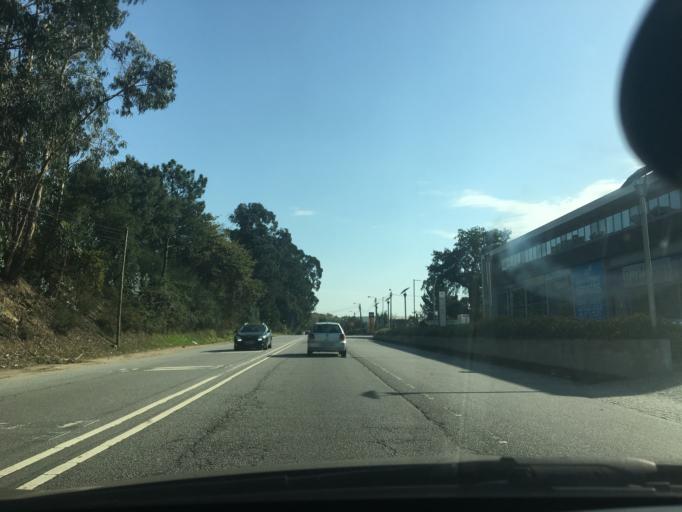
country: PT
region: Porto
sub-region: Maia
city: Maia
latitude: 41.2338
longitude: -8.6390
